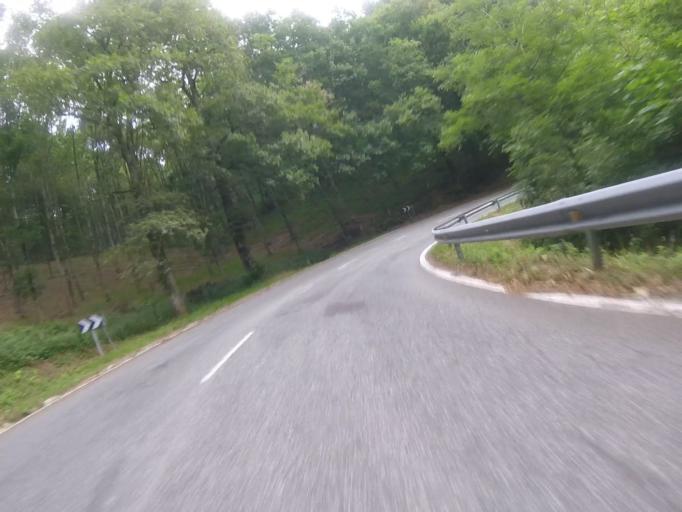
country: ES
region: Navarre
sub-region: Provincia de Navarra
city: Ezkurra
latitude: 43.0846
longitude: -1.8514
